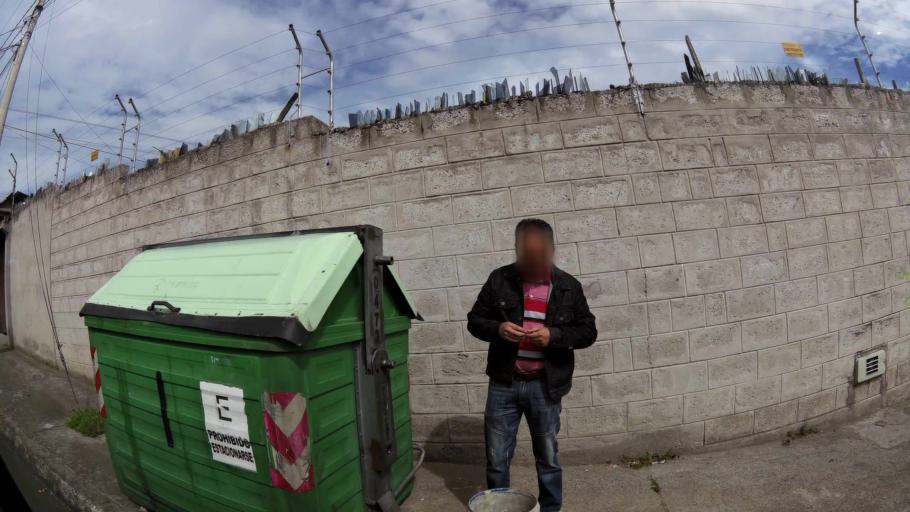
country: EC
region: Tungurahua
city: Ambato
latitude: -1.2436
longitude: -78.6205
